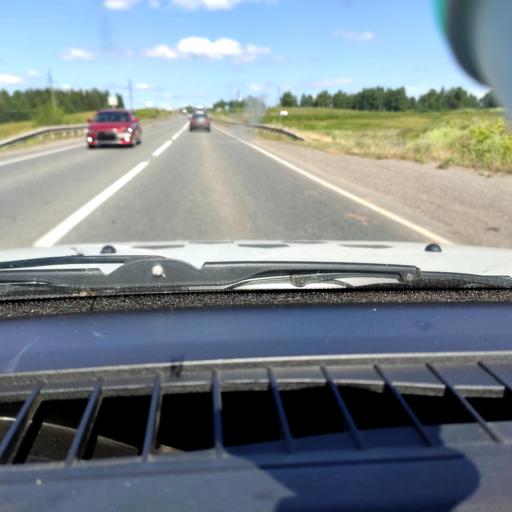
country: RU
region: Udmurtiya
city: Votkinsk
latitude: 56.9693
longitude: 53.7282
